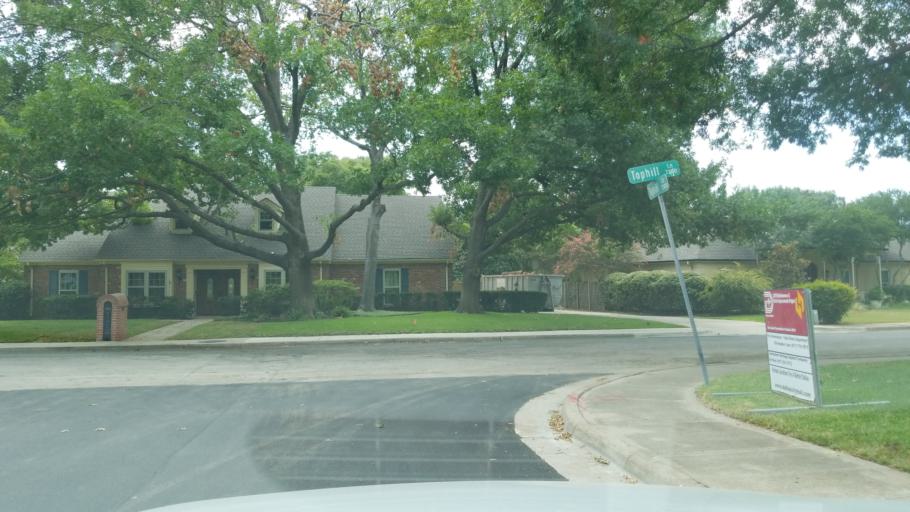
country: US
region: Texas
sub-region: Dallas County
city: Addison
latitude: 32.9532
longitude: -96.7825
